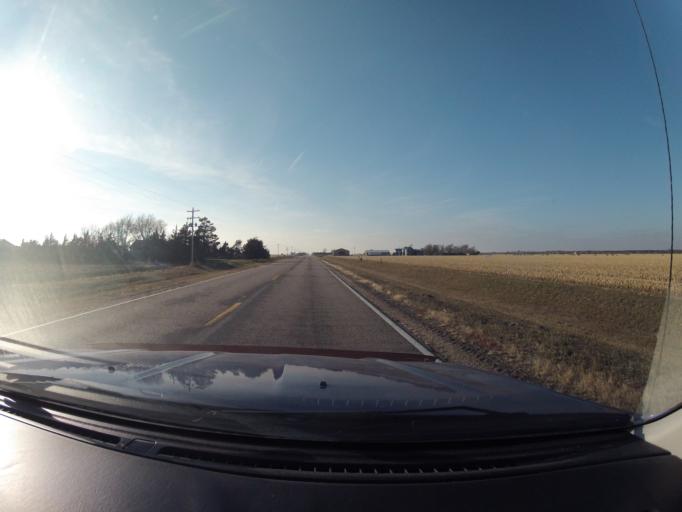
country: US
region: Nebraska
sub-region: Buffalo County
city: Kearney
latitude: 40.6410
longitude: -99.0092
